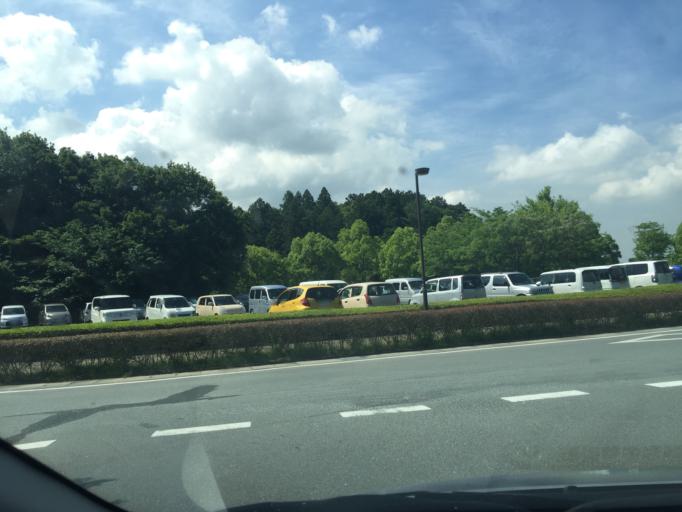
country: JP
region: Shizuoka
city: Kakegawa
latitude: 34.7851
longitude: 138.0024
